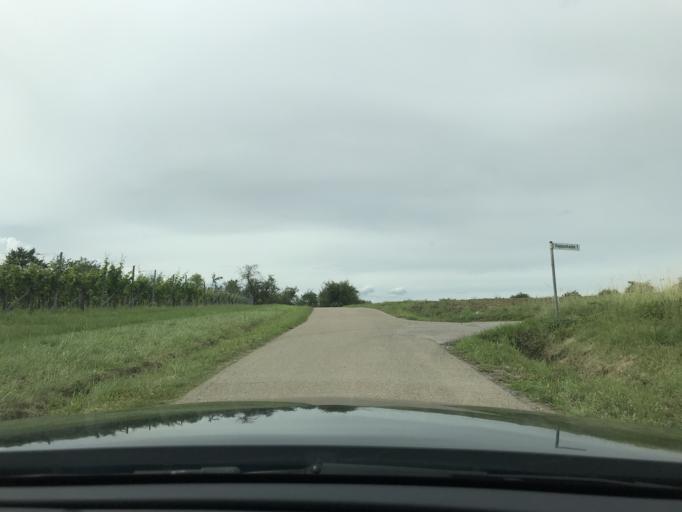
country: DE
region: Baden-Wuerttemberg
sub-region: Regierungsbezirk Stuttgart
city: Weinstadt-Endersbach
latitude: 48.7987
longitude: 9.3610
